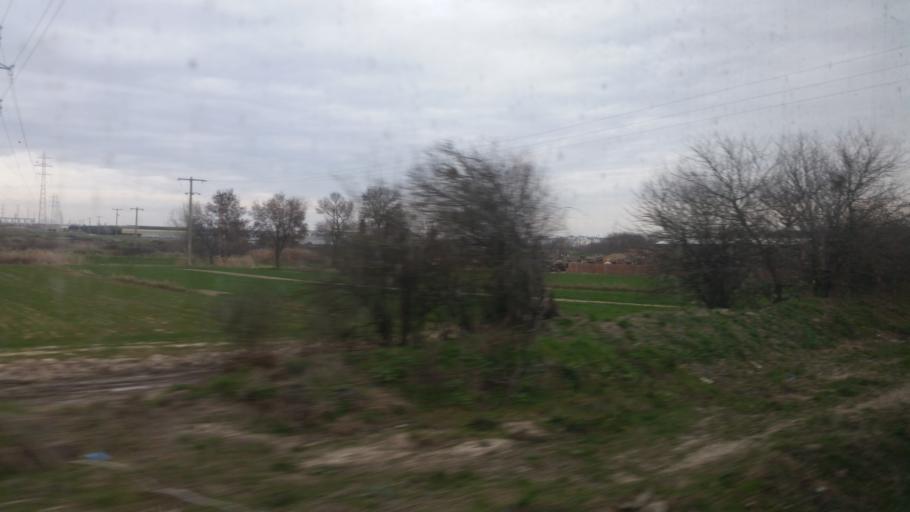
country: TR
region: Tekirdag
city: Velimese
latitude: 41.2566
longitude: 27.9110
